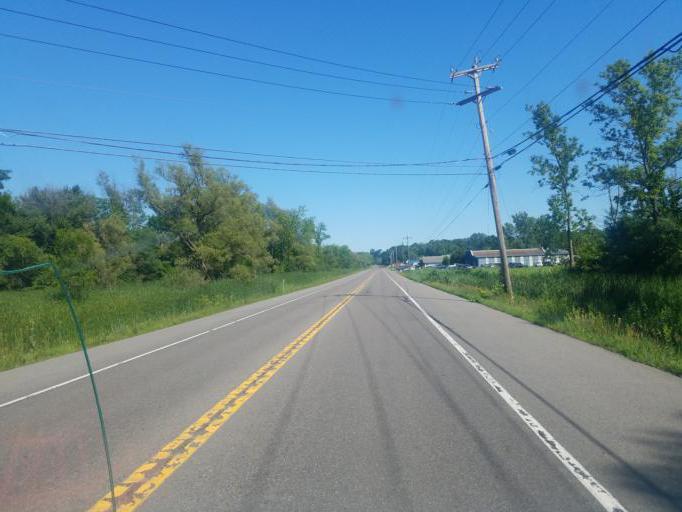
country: US
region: New York
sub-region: Wayne County
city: Lyons
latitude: 43.0646
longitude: -77.0255
